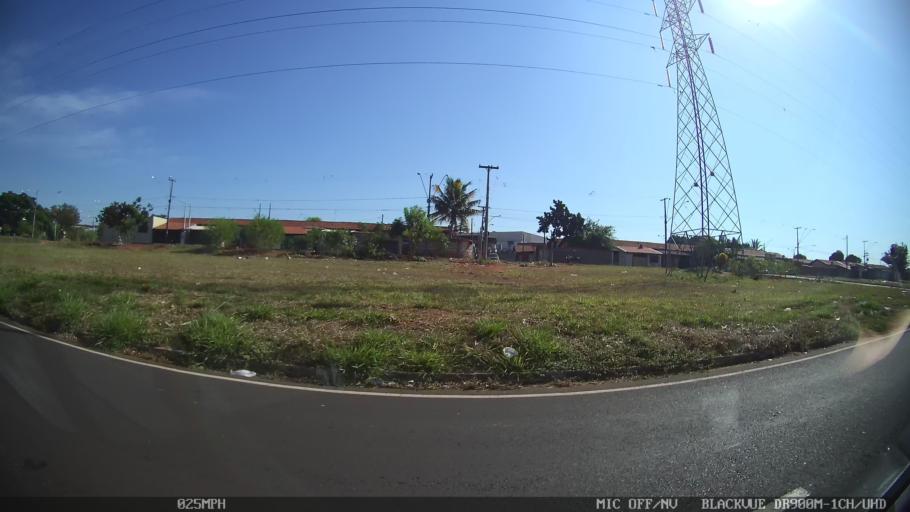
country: BR
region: Sao Paulo
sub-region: Sao Jose Do Rio Preto
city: Sao Jose do Rio Preto
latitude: -20.7666
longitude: -49.3832
